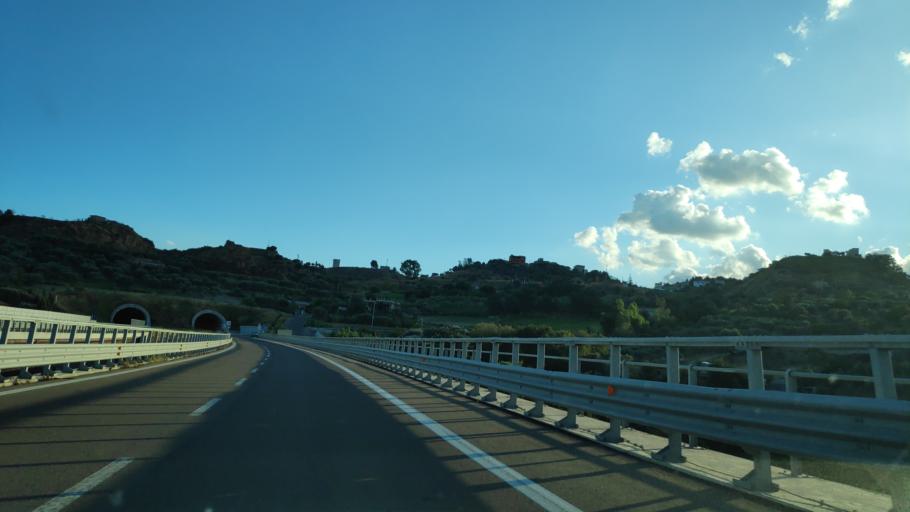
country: IT
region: Calabria
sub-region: Provincia di Reggio Calabria
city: Siderno
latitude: 38.2907
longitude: 16.2807
